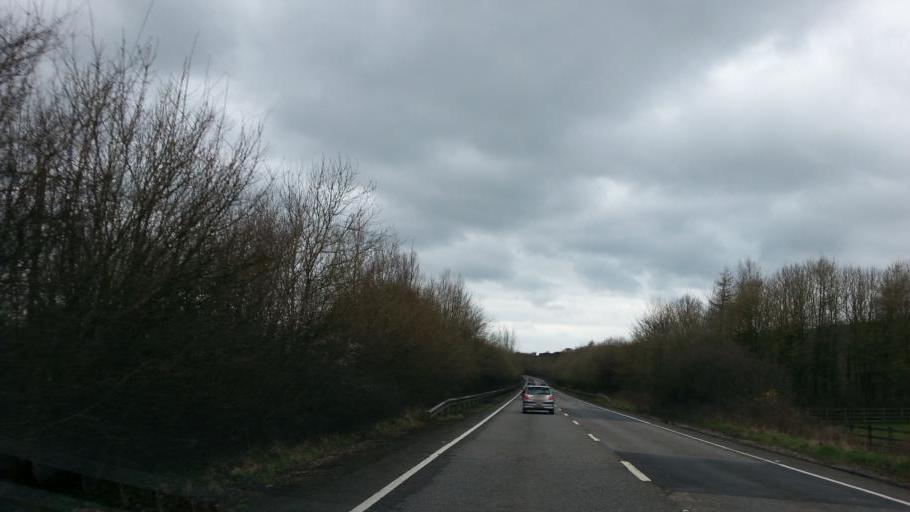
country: GB
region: England
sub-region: Devon
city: Barnstaple
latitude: 51.0645
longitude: -3.9906
